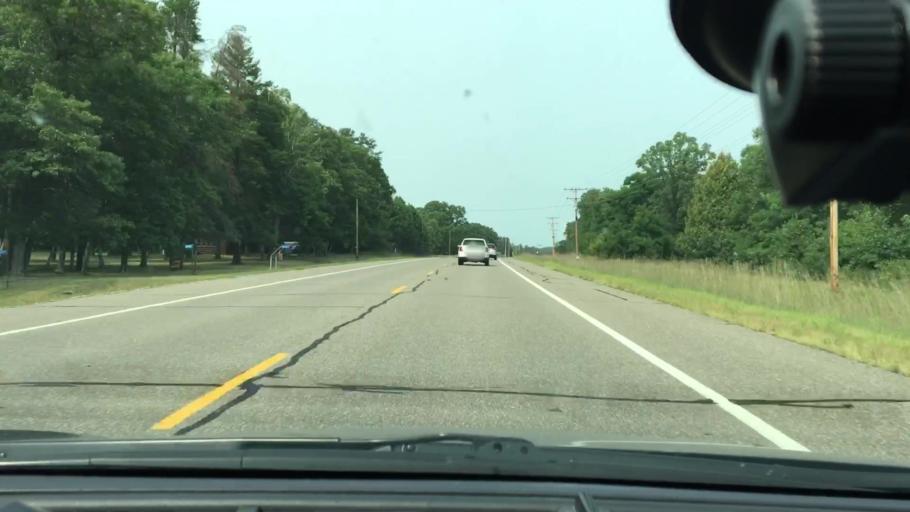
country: US
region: Minnesota
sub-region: Crow Wing County
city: Cross Lake
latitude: 46.6085
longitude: -94.1316
